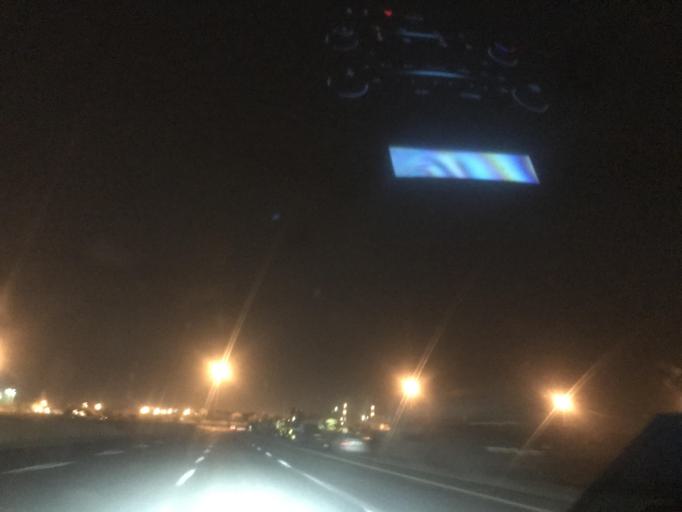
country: SA
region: Ar Riyad
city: Riyadh
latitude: 24.7607
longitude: 46.5829
